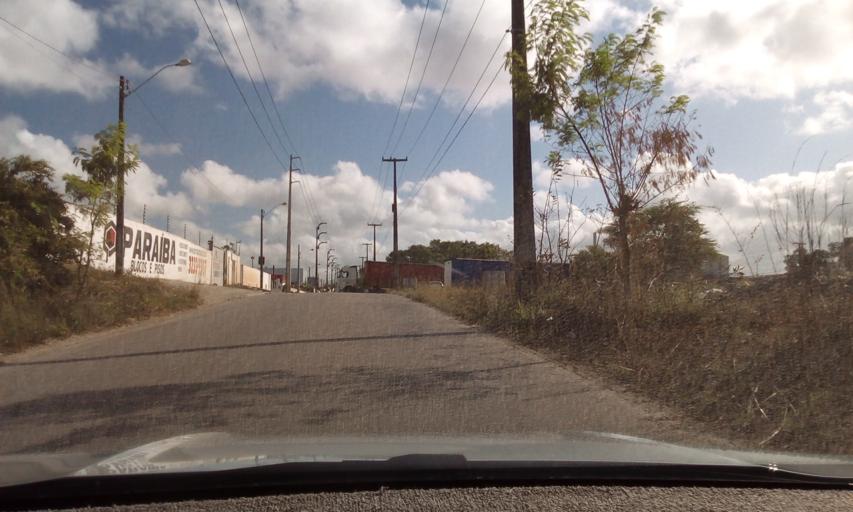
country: BR
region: Paraiba
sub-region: Bayeux
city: Bayeux
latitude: -7.1710
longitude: -34.9063
